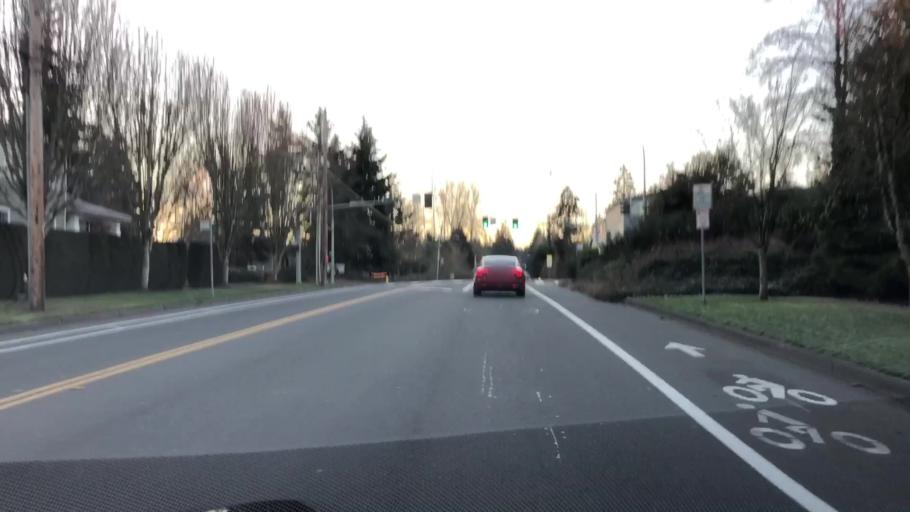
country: US
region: Washington
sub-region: King County
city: Kirkland
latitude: 47.6902
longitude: -122.1758
